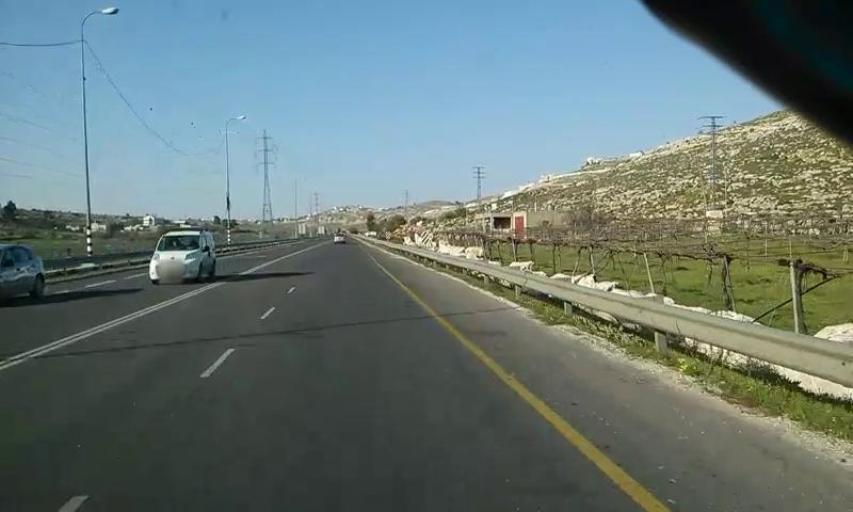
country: PS
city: Al Buq`ah
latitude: 31.5432
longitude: 35.1333
